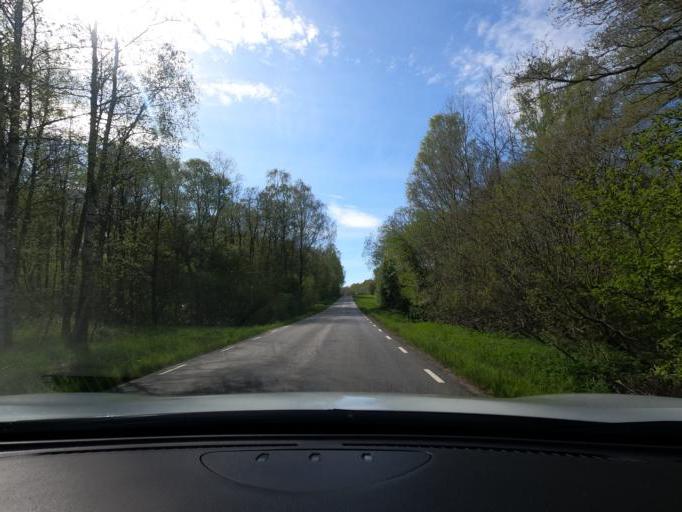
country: SE
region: Vaestra Goetaland
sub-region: Marks Kommun
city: Kinna
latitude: 57.4751
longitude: 12.5903
